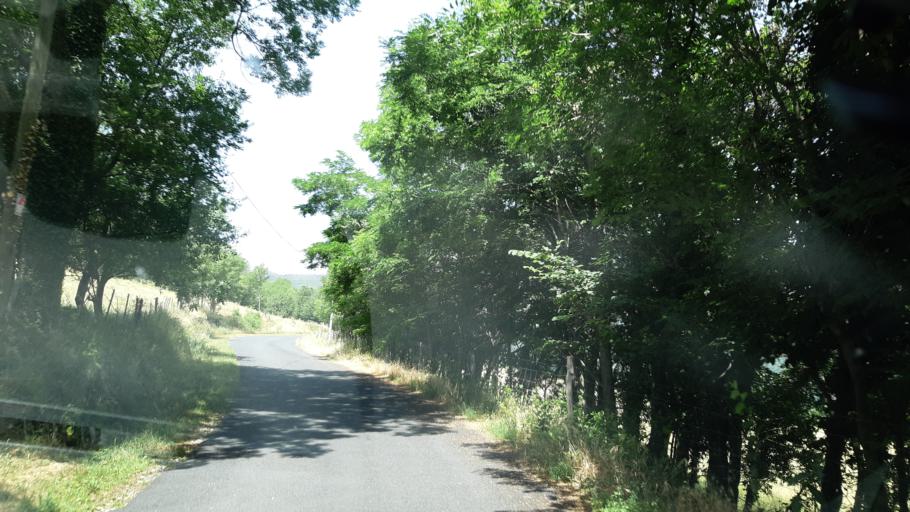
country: FR
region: Languedoc-Roussillon
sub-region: Departement des Pyrenees-Orientales
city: Arles
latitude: 42.5478
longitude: 2.5859
